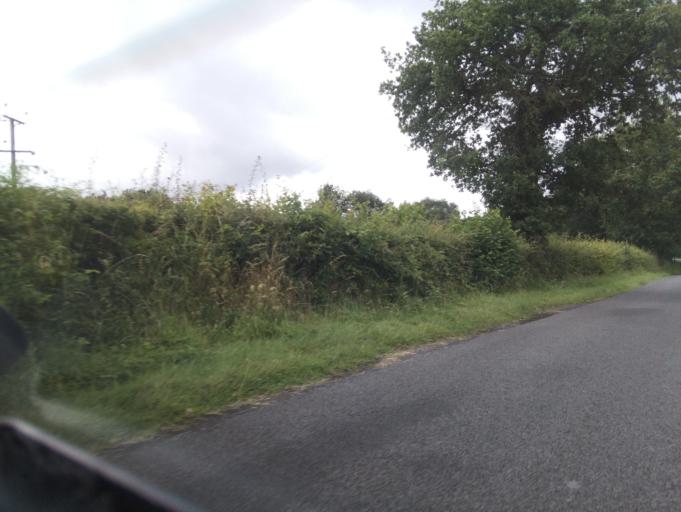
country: GB
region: England
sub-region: Solihull
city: Dickens Heath
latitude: 52.3793
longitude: -1.8409
